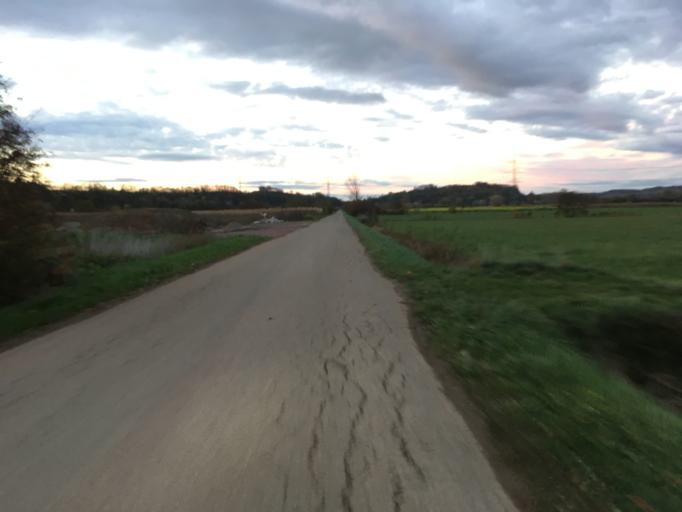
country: DE
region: Baden-Wuerttemberg
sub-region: Freiburg Region
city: Bahlingen
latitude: 48.1298
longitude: 7.7433
